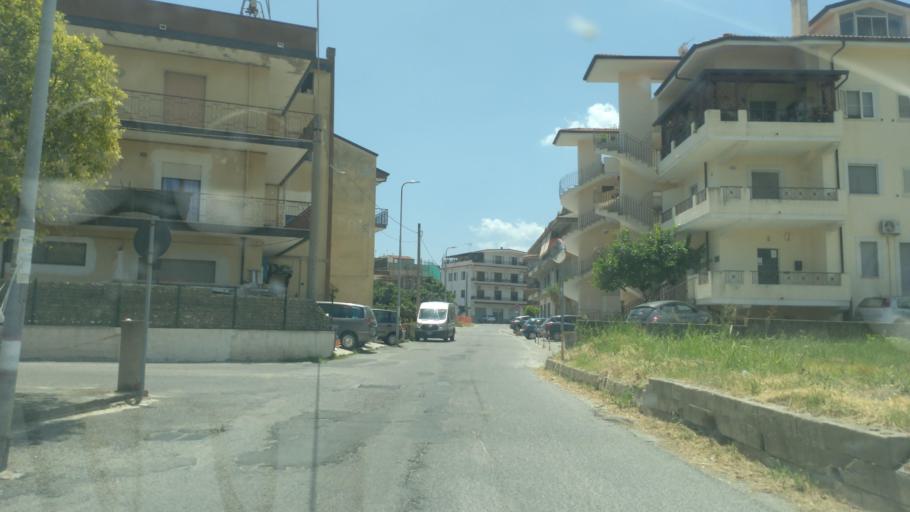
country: IT
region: Calabria
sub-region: Provincia di Catanzaro
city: Marina di Davoli
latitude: 38.6686
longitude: 16.5425
